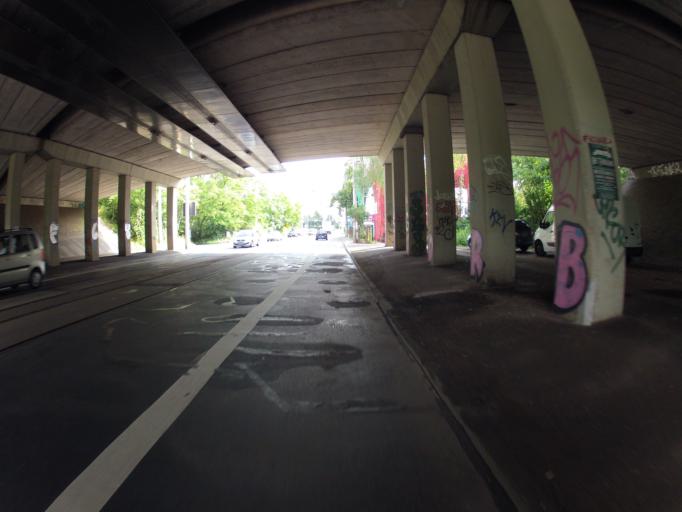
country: DE
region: Saxony
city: Markkleeberg
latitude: 51.3018
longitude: 12.3733
